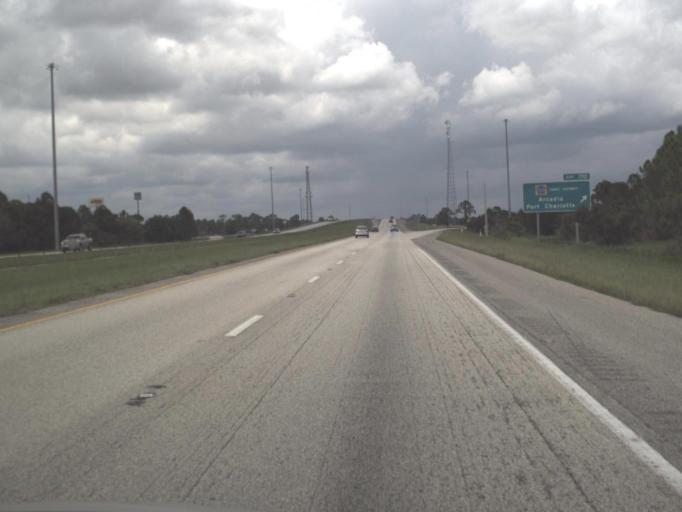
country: US
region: Florida
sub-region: Charlotte County
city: Harbour Heights
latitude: 27.0149
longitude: -82.0449
